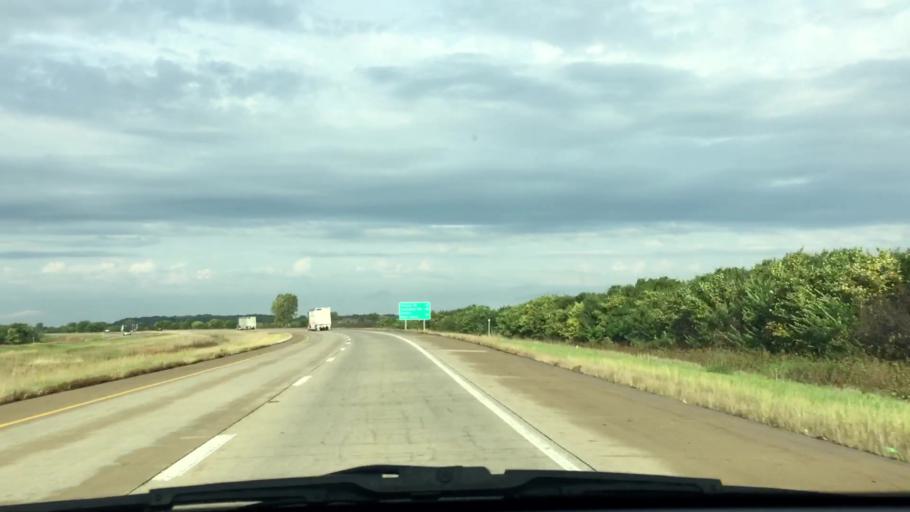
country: US
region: Illinois
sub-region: Whiteside County
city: Sterling
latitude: 41.7644
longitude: -89.7956
